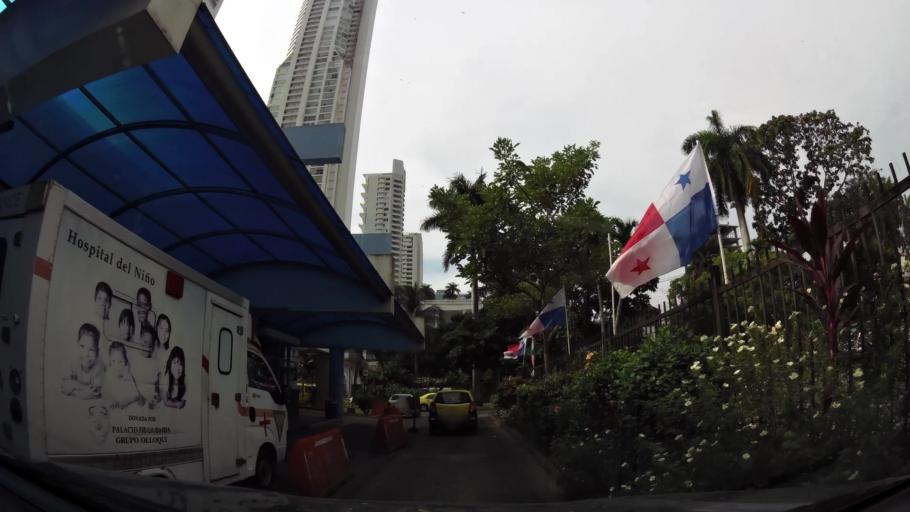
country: PA
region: Panama
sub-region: Distrito de Panama
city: Ancon
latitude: 8.9686
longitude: -79.5333
